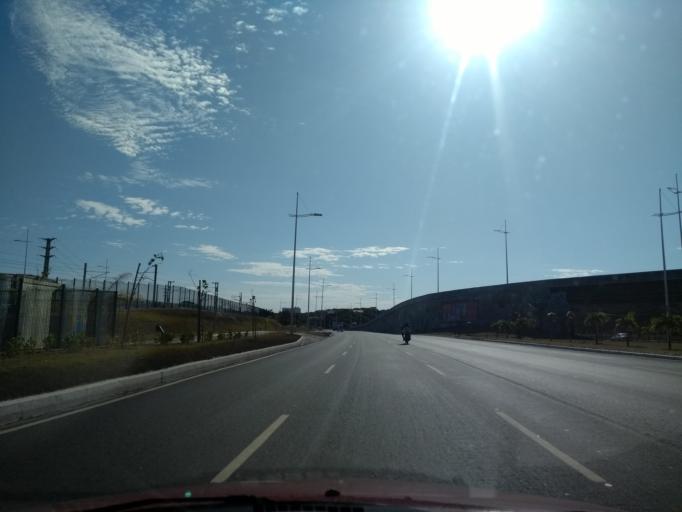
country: BR
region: Bahia
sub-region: Lauro De Freitas
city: Lauro de Freitas
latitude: -12.9258
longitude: -38.3831
